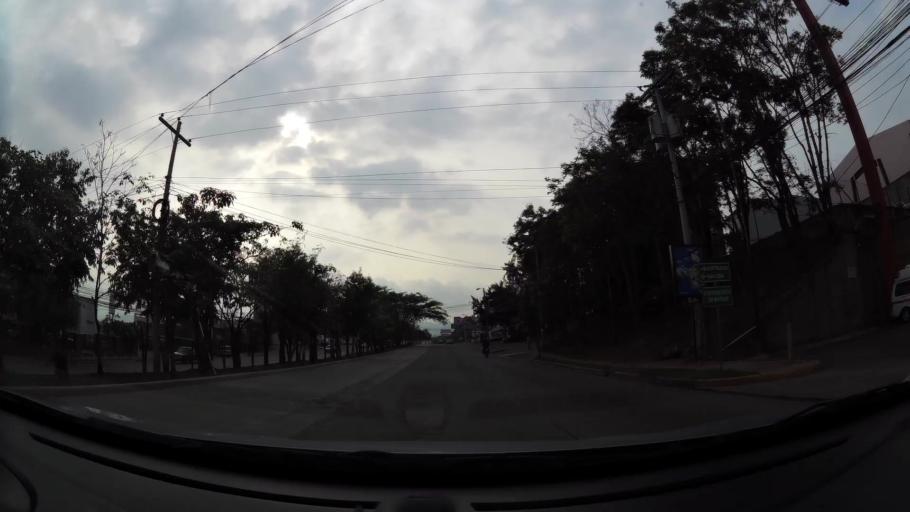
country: HN
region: Francisco Morazan
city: Tegucigalpa
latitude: 14.0846
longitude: -87.1824
